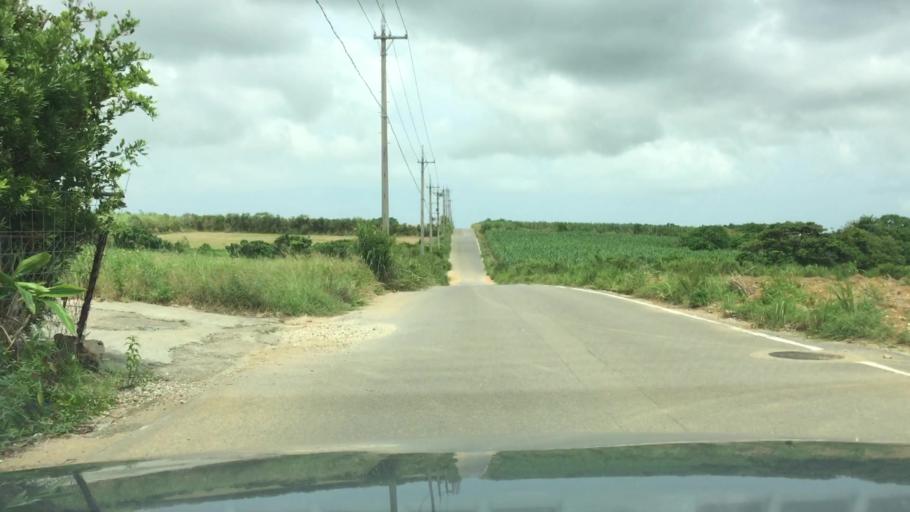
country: JP
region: Okinawa
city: Ishigaki
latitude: 24.3955
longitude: 124.1790
